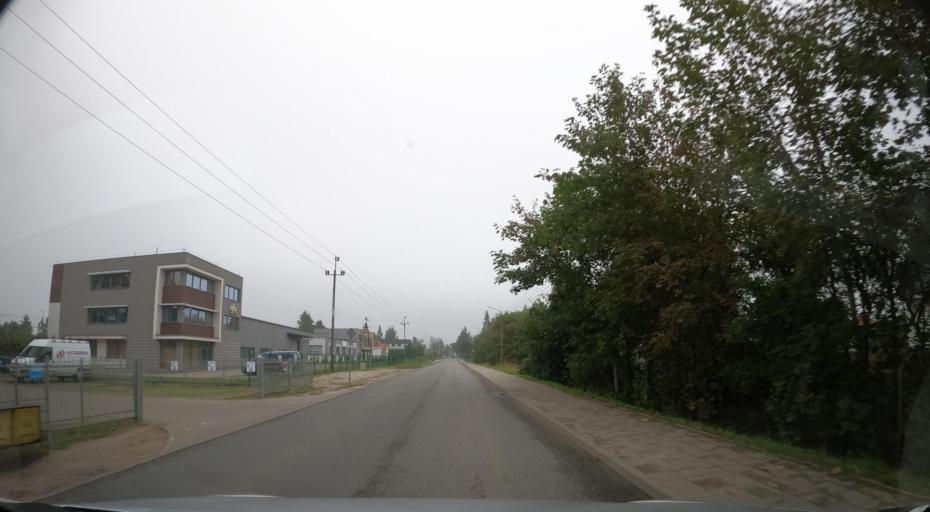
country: PL
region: Pomeranian Voivodeship
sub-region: Powiat kartuski
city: Chwaszczyno
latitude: 54.4234
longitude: 18.4556
